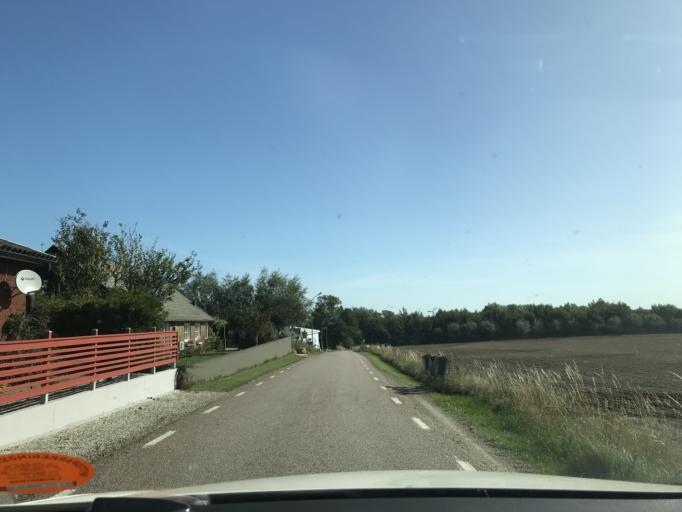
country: SE
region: Skane
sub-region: Landskrona
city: Asmundtorp
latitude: 55.9072
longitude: 12.9396
